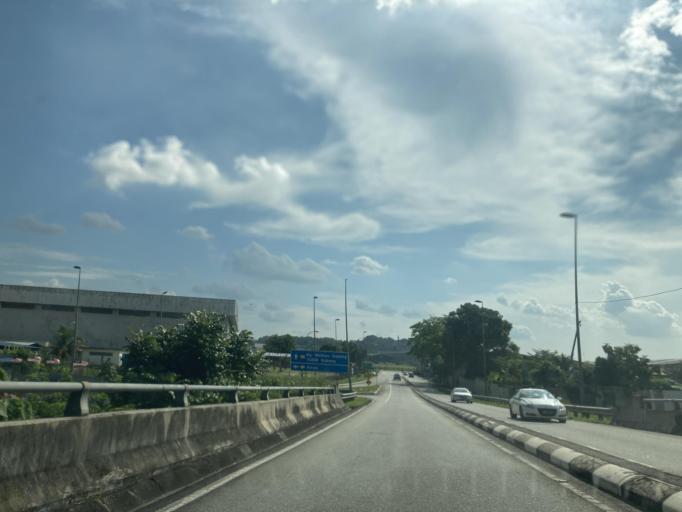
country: MY
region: Selangor
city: Kampung Baru Subang
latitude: 3.1400
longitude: 101.5503
